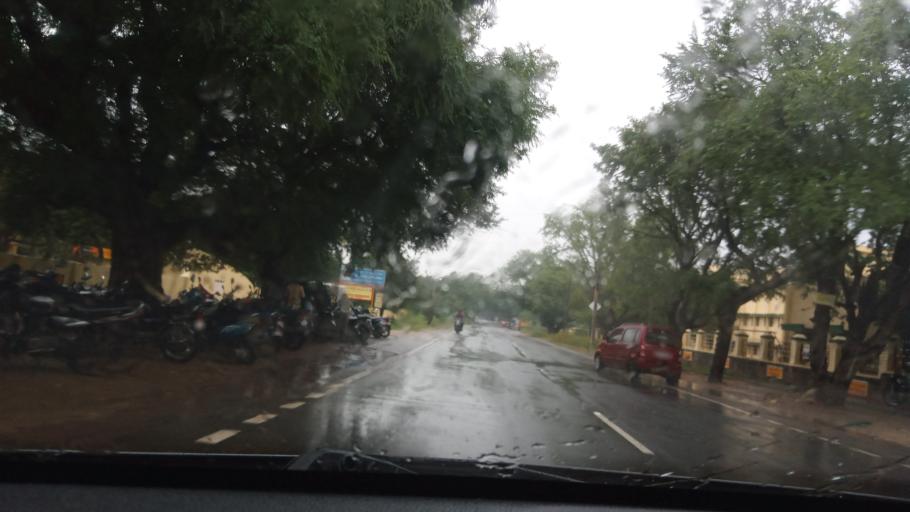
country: IN
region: Tamil Nadu
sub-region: Vellore
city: Kalavai
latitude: 12.8029
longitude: 79.4315
